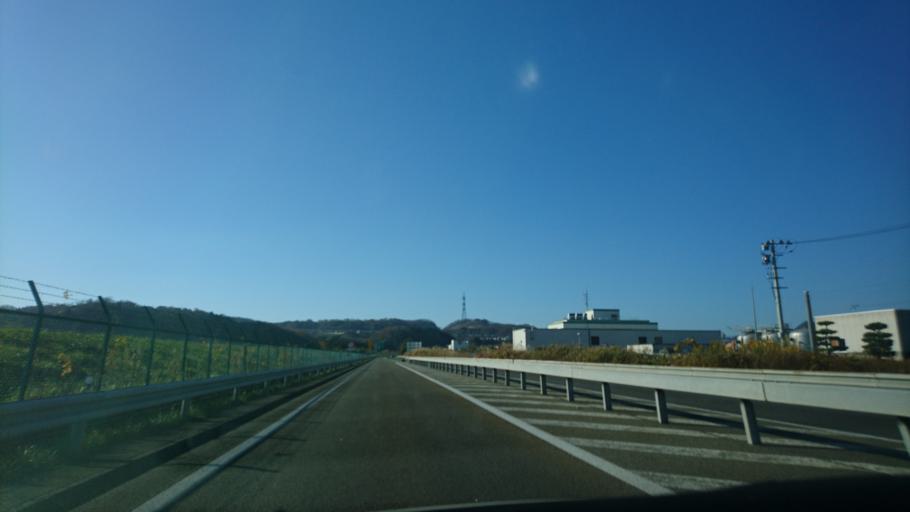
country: JP
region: Miyagi
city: Sendai
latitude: 38.2068
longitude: 140.8561
